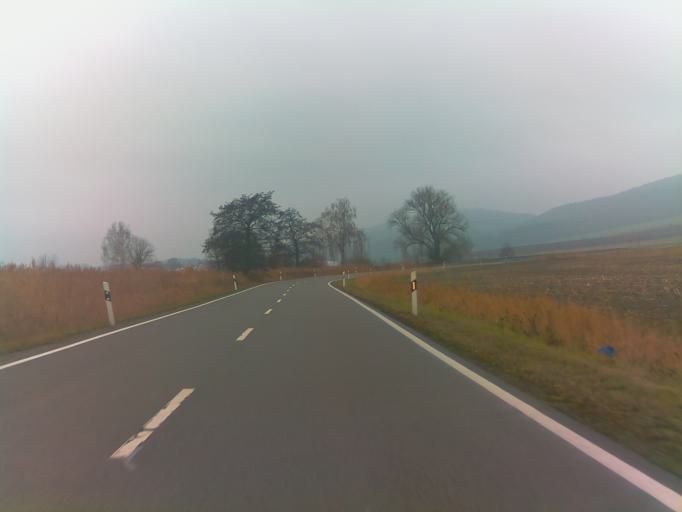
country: DE
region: Thuringia
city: Romhild
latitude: 50.4254
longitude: 10.5139
